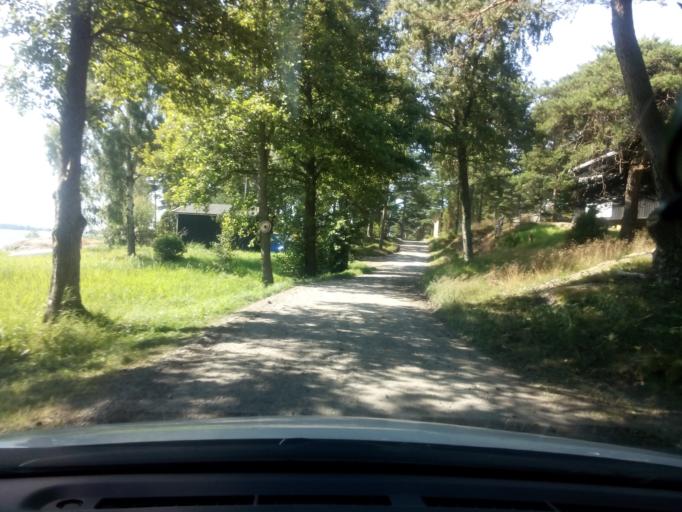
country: SE
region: Soedermanland
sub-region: Oxelosunds Kommun
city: Oxelosund
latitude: 58.7258
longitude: 17.2472
